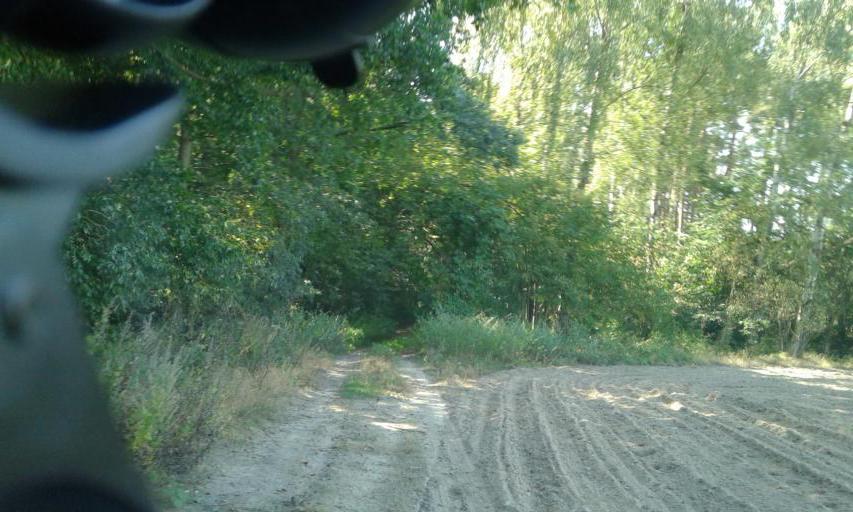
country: PL
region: West Pomeranian Voivodeship
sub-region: Powiat choszczenski
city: Krzecin
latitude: 53.0705
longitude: 15.5444
